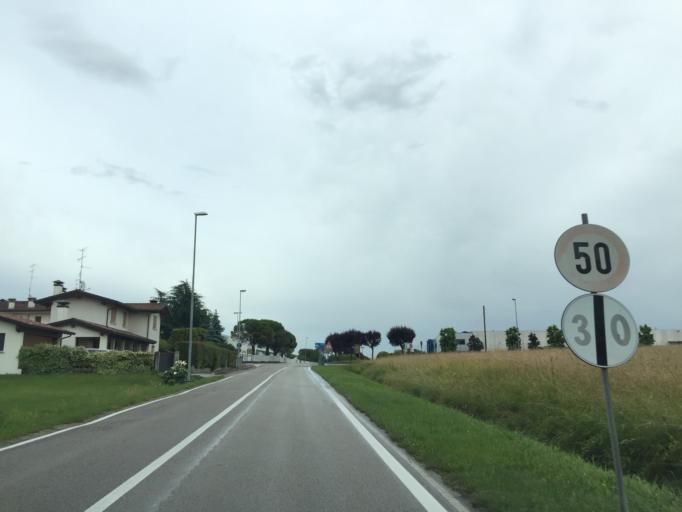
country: IT
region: Friuli Venezia Giulia
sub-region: Provincia di Pordenone
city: Porcia
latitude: 45.9578
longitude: 12.5920
